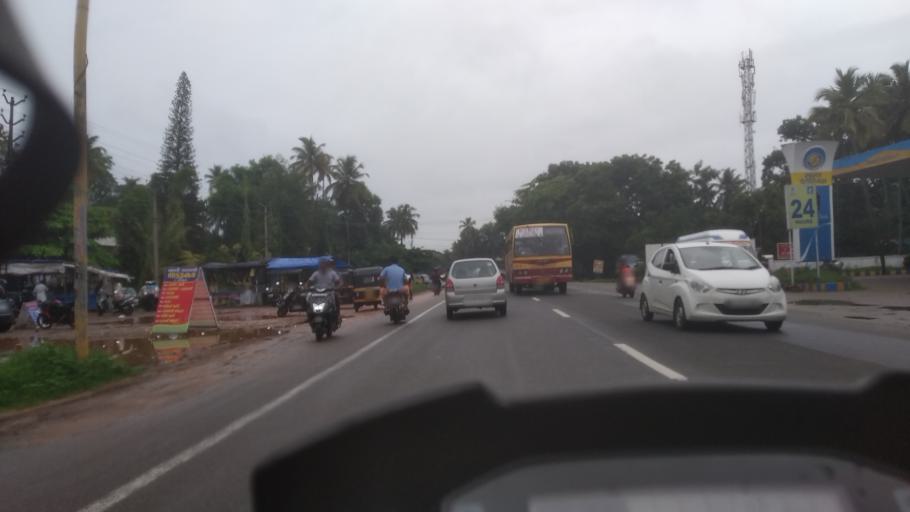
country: IN
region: Kerala
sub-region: Alappuzha
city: Kayankulam
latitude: 9.1568
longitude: 76.5092
